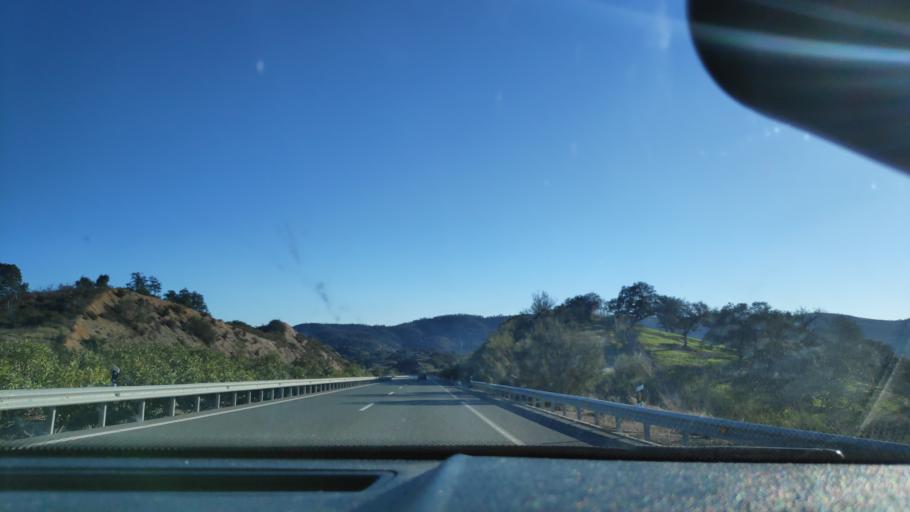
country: ES
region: Andalusia
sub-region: Provincia de Sevilla
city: El Ronquillo
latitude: 37.6879
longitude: -6.1831
